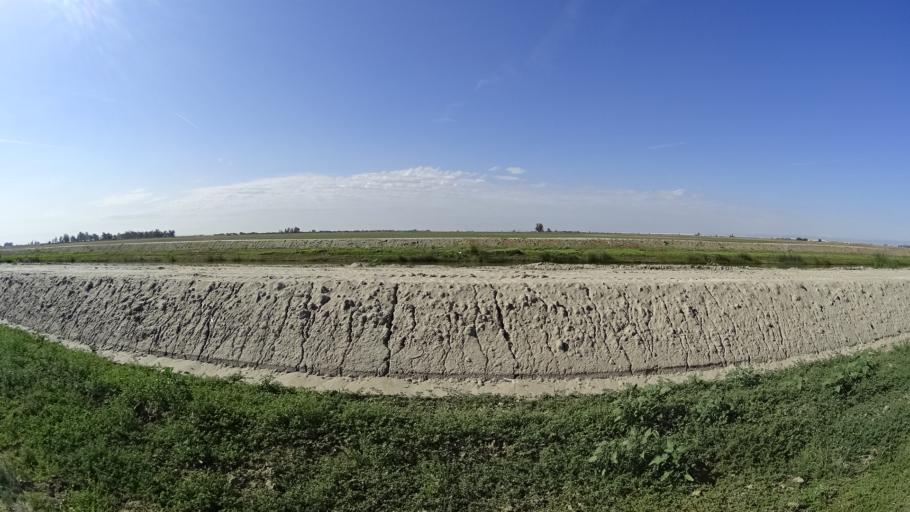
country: US
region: California
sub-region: Kings County
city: Home Garden
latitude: 36.2258
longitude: -119.6697
